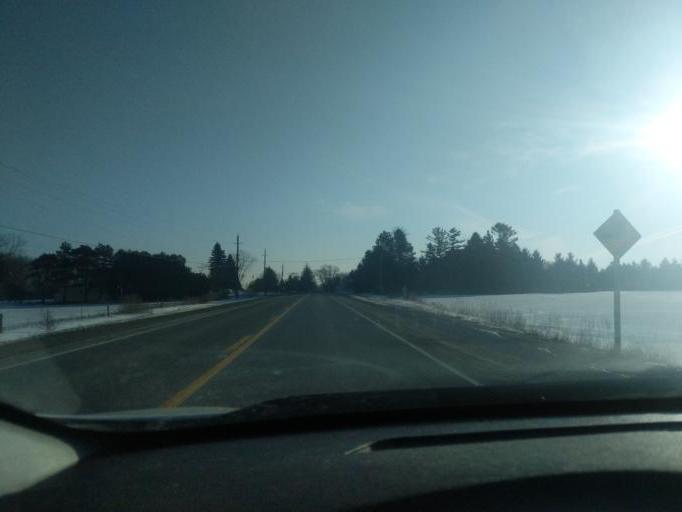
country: CA
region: Ontario
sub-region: Oxford County
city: Woodstock
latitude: 43.2700
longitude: -80.6665
